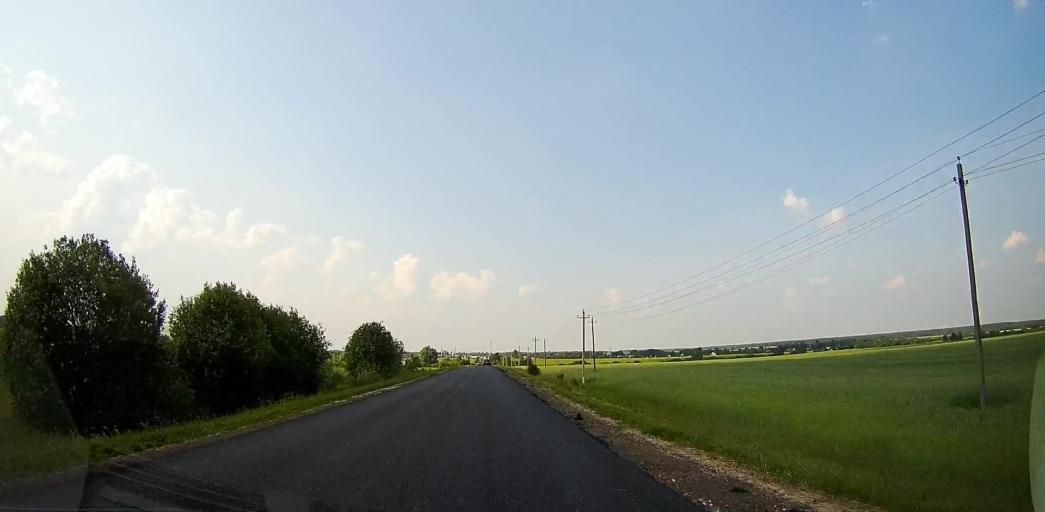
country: RU
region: Moskovskaya
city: Barybino
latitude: 55.2377
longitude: 37.9195
